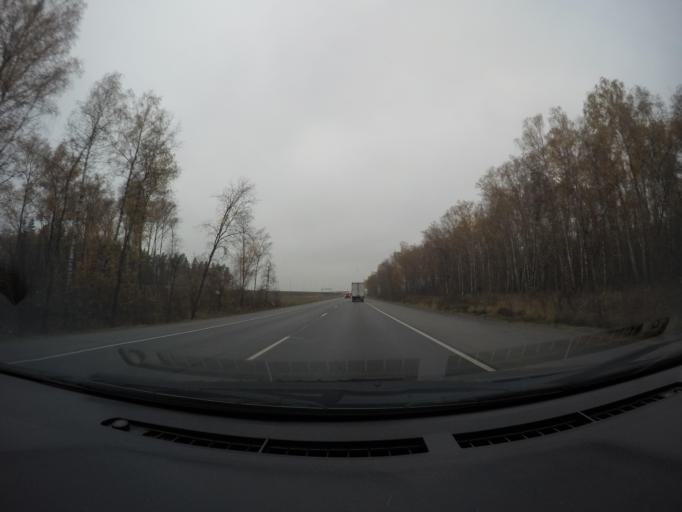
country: RU
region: Moskovskaya
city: Belyye Stolby
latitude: 55.3476
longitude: 37.8808
